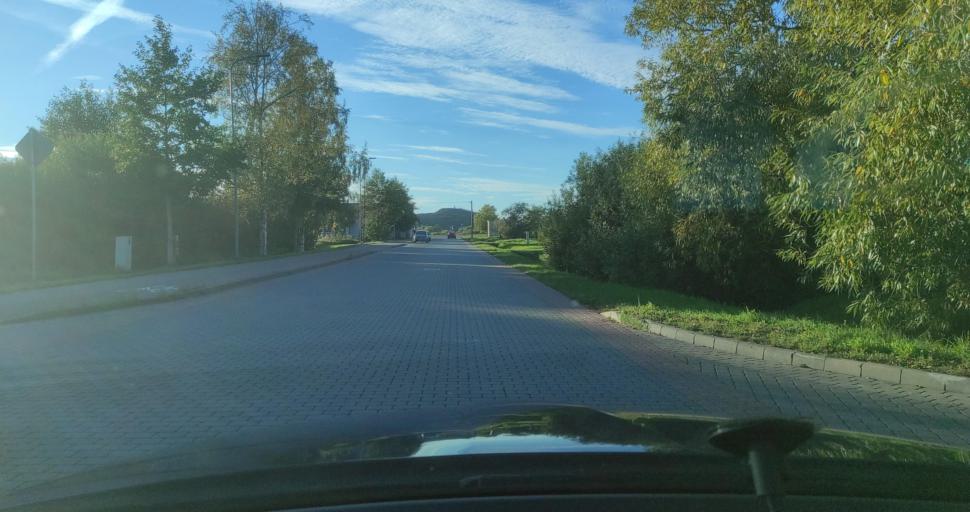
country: LV
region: Ventspils
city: Ventspils
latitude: 57.3670
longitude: 21.5678
